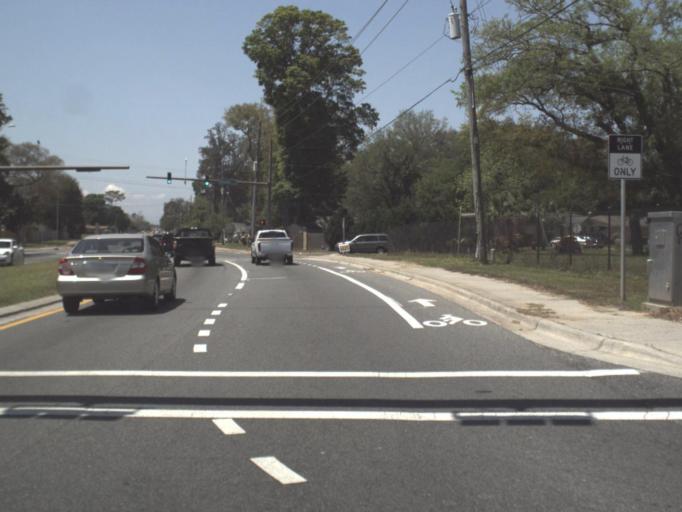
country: US
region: Florida
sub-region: Escambia County
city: Brent
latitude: 30.4814
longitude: -87.2316
